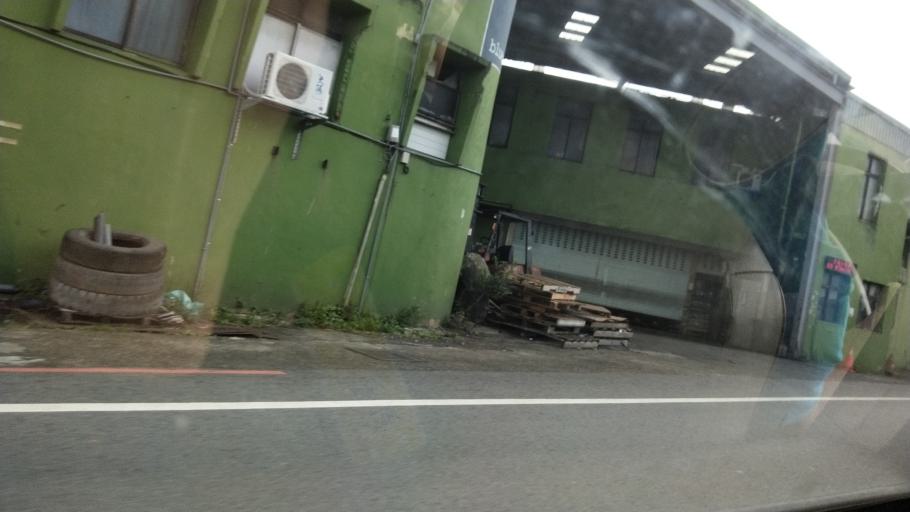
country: TW
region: Taiwan
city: Taoyuan City
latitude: 25.0064
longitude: 121.1313
